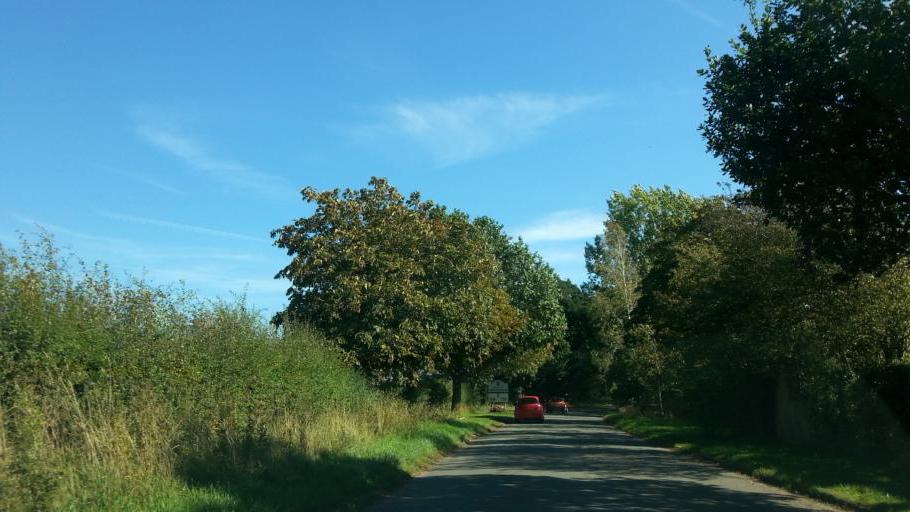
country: GB
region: England
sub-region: Staffordshire
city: Stafford
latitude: 52.8041
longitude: -2.1707
